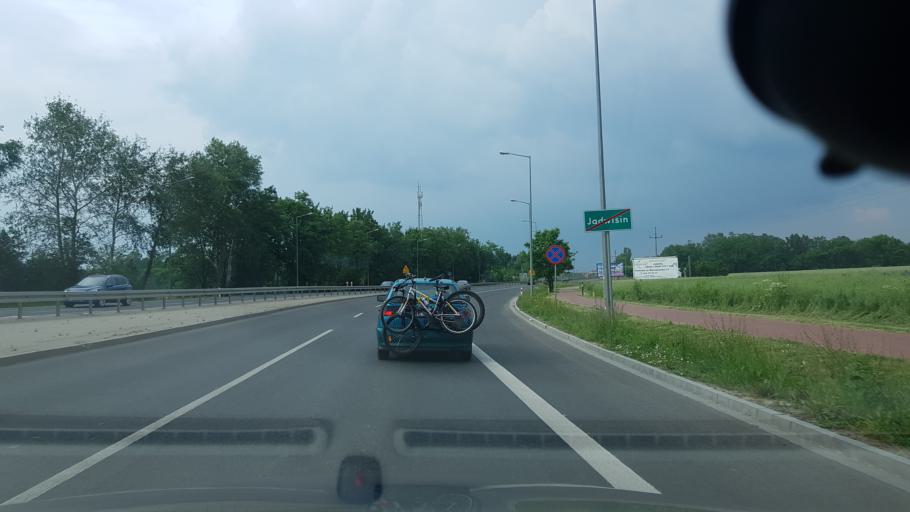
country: PL
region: Masovian Voivodeship
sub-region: Powiat legionowski
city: Bialobrzegi
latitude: 52.4719
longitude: 21.0293
